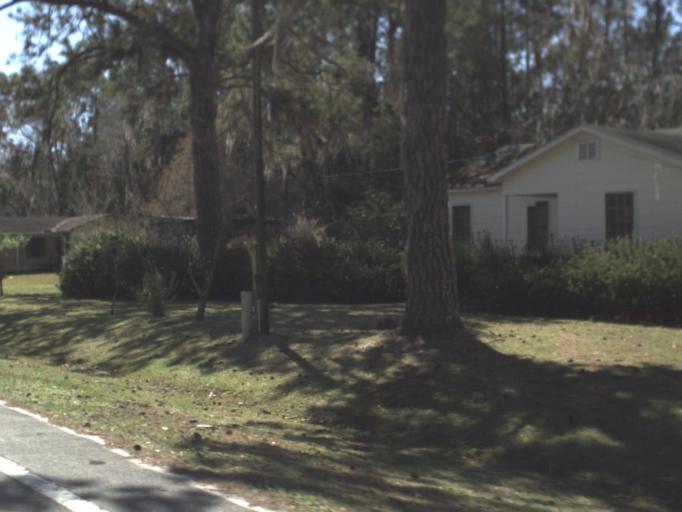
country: US
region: Florida
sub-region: Leon County
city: Woodville
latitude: 30.1595
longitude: -84.2055
